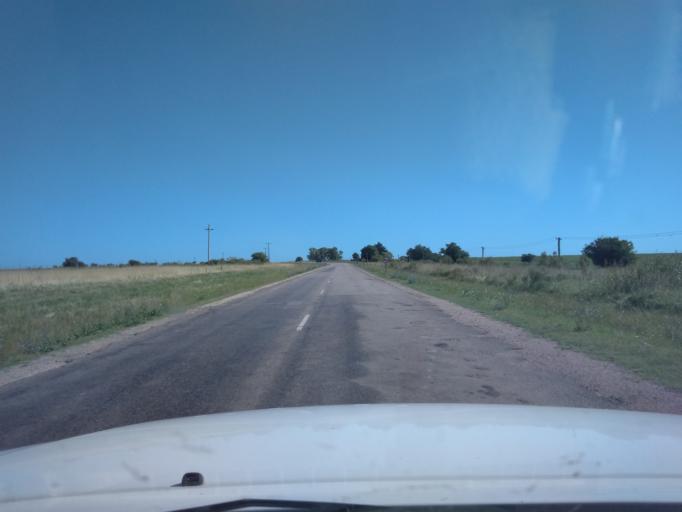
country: UY
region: Canelones
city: San Ramon
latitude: -34.2146
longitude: -55.9295
